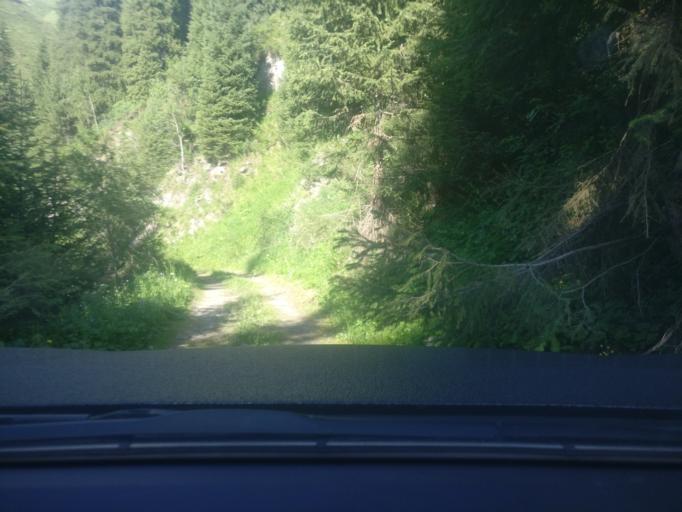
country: KZ
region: Almaty Qalasy
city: Almaty
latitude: 43.1061
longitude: 76.9529
